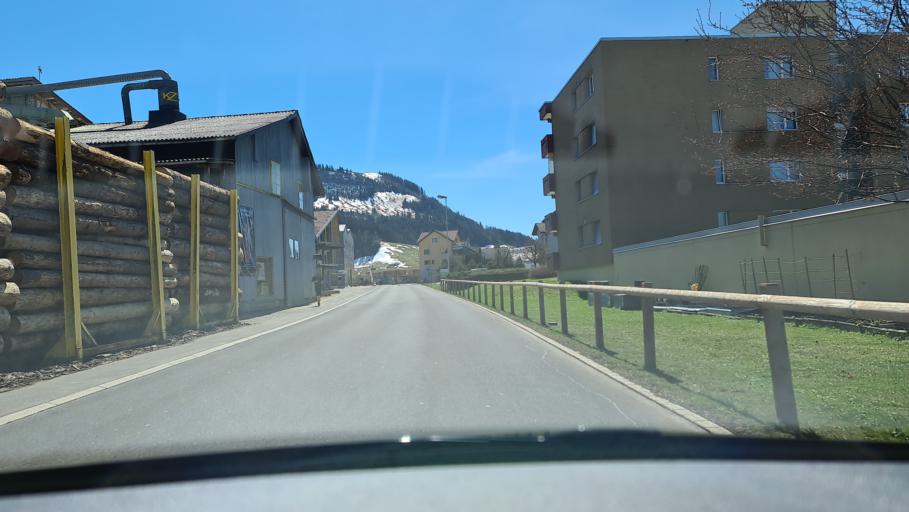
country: CH
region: Schwyz
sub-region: Bezirk Einsiedeln
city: Einsiedeln
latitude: 47.1229
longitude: 8.7428
